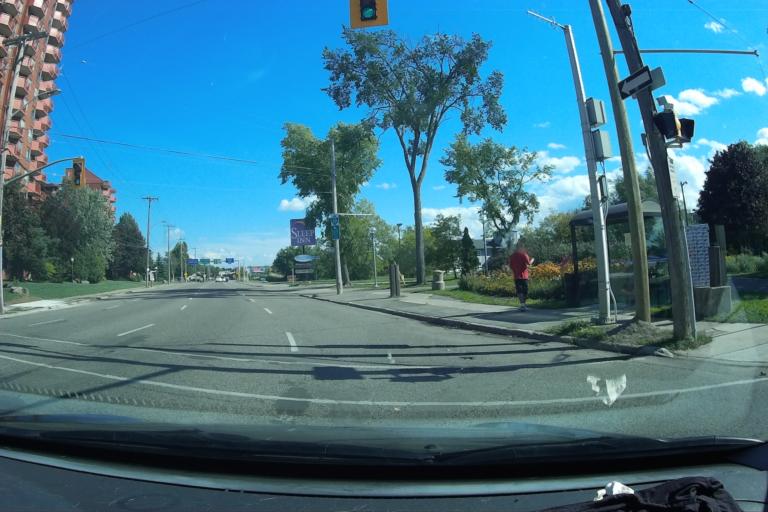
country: CA
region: Ontario
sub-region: Algoma
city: Sault Ste. Marie
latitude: 46.5069
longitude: -84.3293
